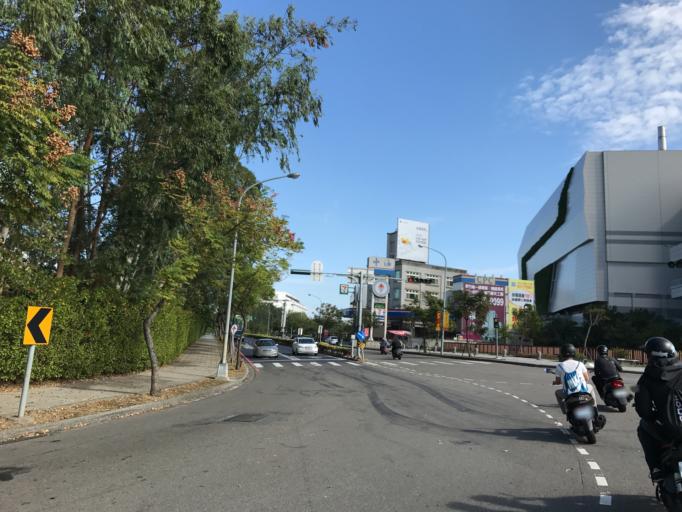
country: TW
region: Taiwan
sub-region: Hsinchu
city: Hsinchu
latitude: 24.7714
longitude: 121.0089
